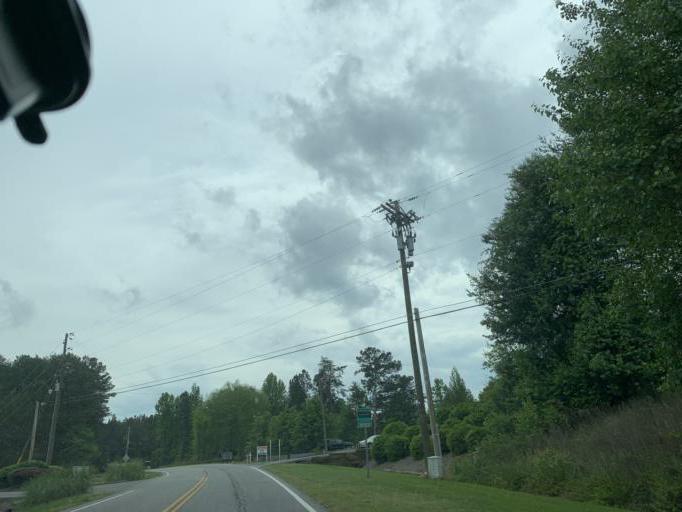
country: US
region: Georgia
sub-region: Forsyth County
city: Cumming
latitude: 34.2088
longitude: -84.1199
